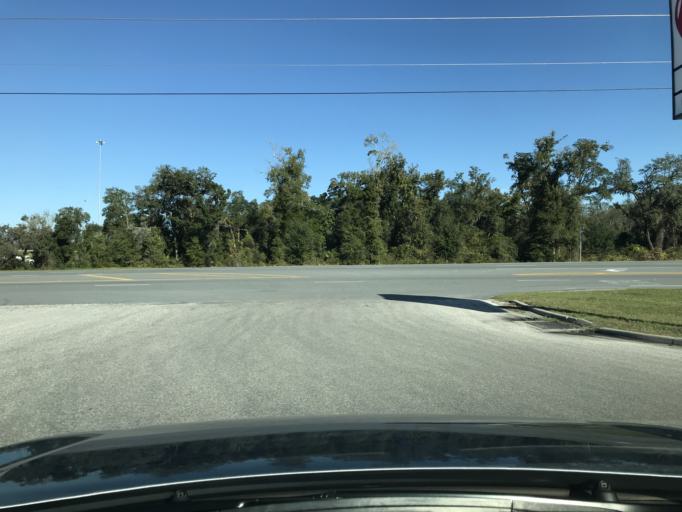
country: US
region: Florida
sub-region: Sumter County
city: Lake Panasoffkee
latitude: 28.7540
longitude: -82.0990
